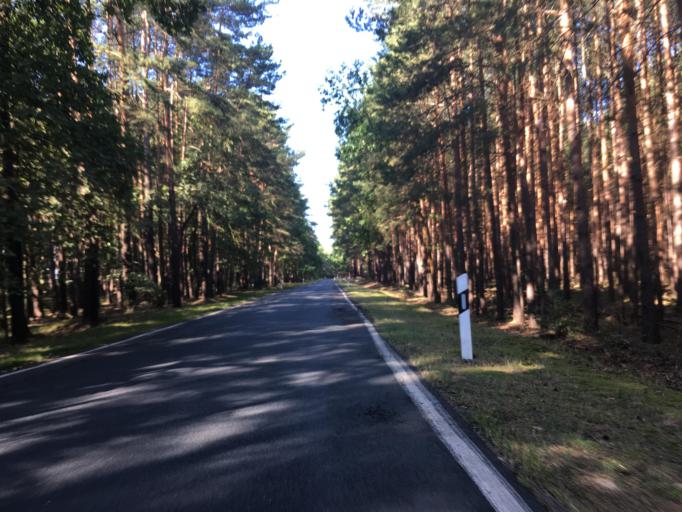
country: DE
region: Brandenburg
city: Storkow
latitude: 52.2459
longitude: 13.8525
